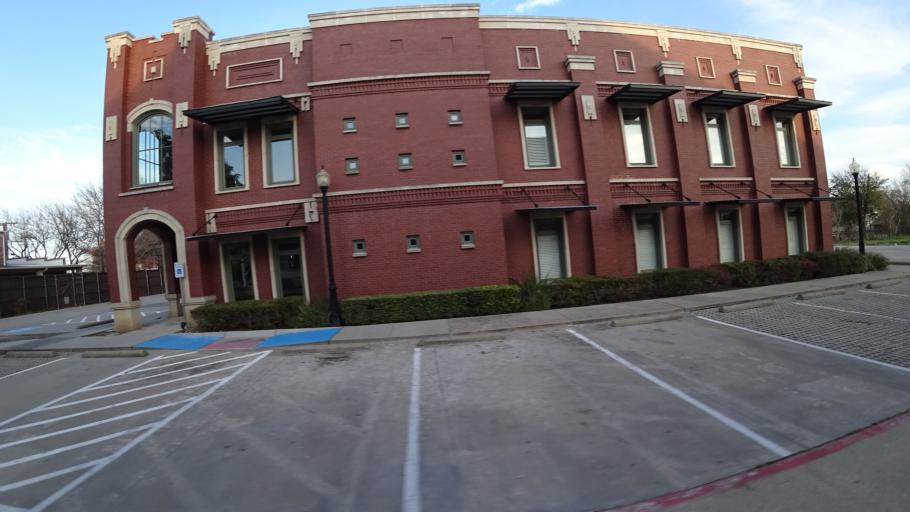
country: US
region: Texas
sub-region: Denton County
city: Lewisville
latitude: 33.0457
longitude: -96.9990
